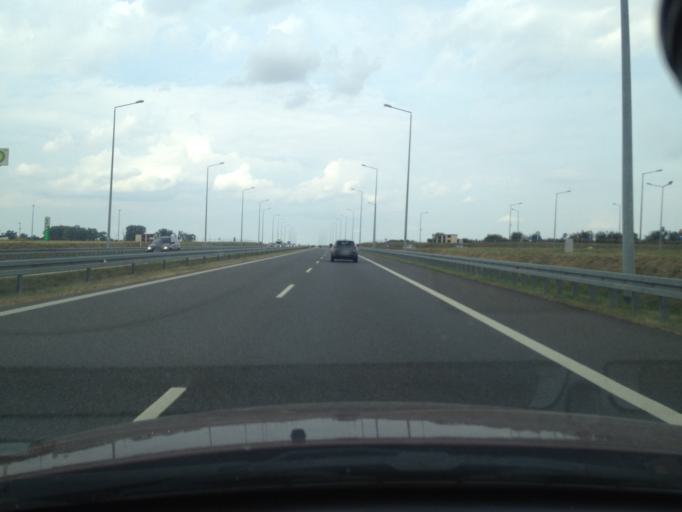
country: PL
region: West Pomeranian Voivodeship
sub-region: Powiat pyrzycki
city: Kozielice
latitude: 53.0515
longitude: 14.8658
